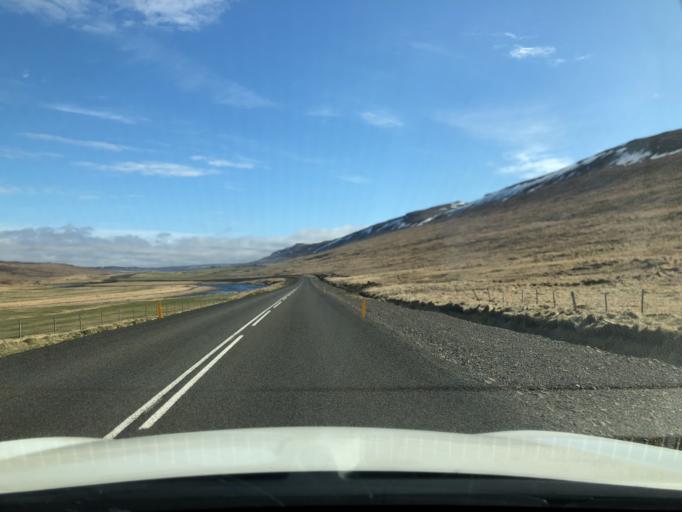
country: IS
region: West
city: Borgarnes
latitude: 65.1370
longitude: -21.6037
